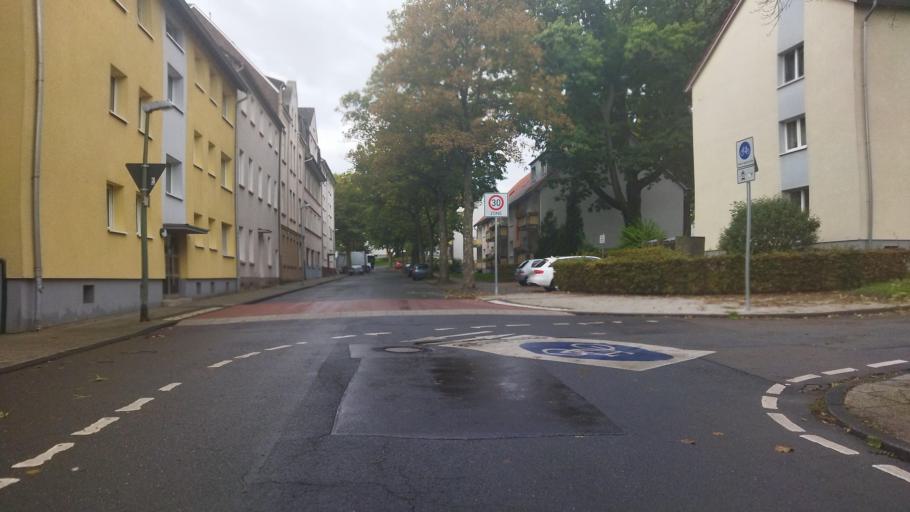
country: DE
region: North Rhine-Westphalia
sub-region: Regierungsbezirk Dusseldorf
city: Essen
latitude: 51.4574
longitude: 7.0766
